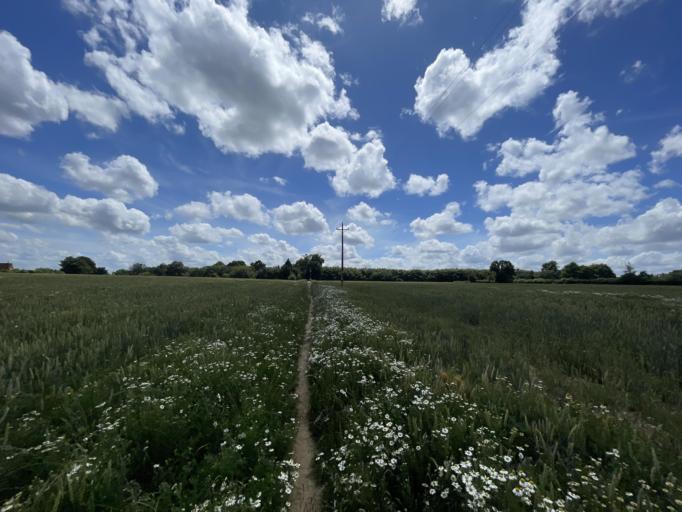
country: GB
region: England
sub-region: Kent
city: Edenbridge
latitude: 51.1650
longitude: 0.1389
